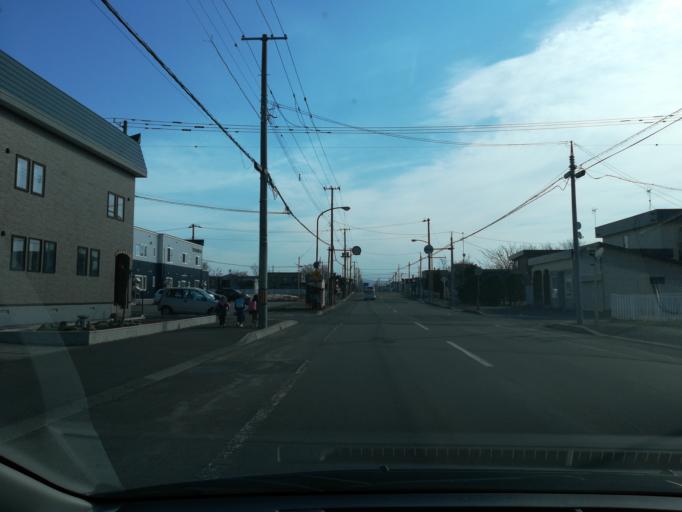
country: JP
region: Hokkaido
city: Iwamizawa
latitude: 43.2030
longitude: 141.7481
